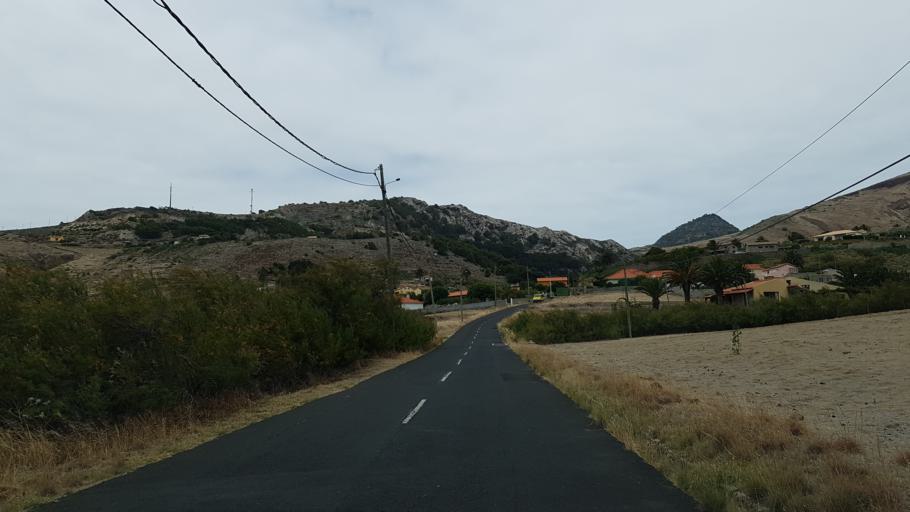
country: PT
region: Madeira
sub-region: Porto Santo
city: Vila de Porto Santo
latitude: 33.0735
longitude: -16.3099
